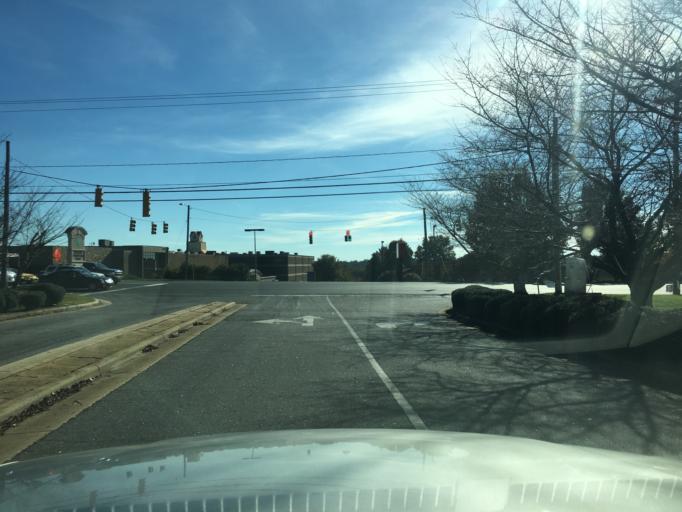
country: US
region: North Carolina
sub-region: Catawba County
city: Hickory
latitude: 35.7045
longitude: -81.2983
